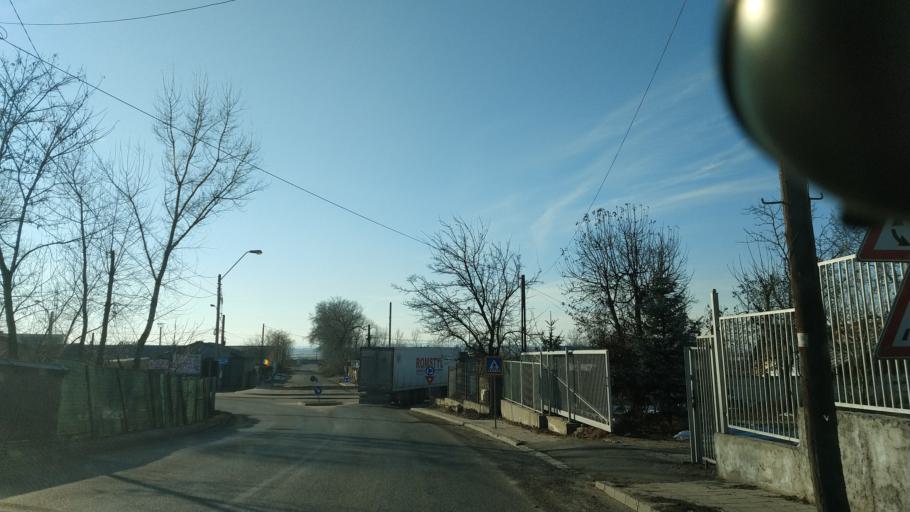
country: RO
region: Neamt
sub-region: Municipiul Roman
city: Roman
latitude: 46.9271
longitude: 26.9095
